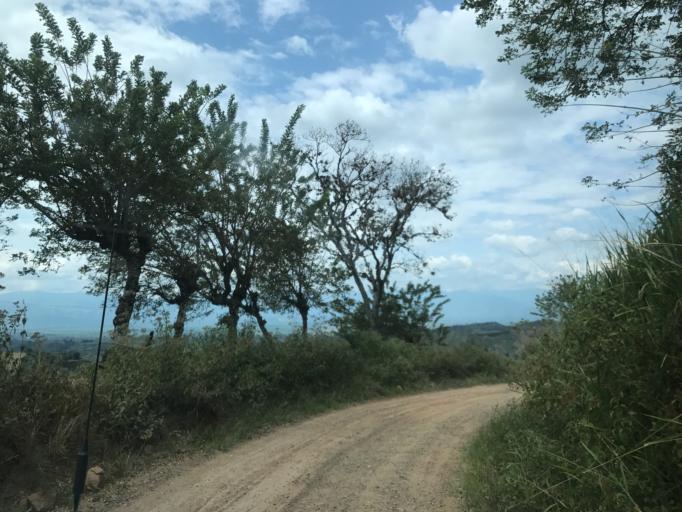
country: CO
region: Valle del Cauca
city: Obando
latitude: 4.5615
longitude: -75.9293
